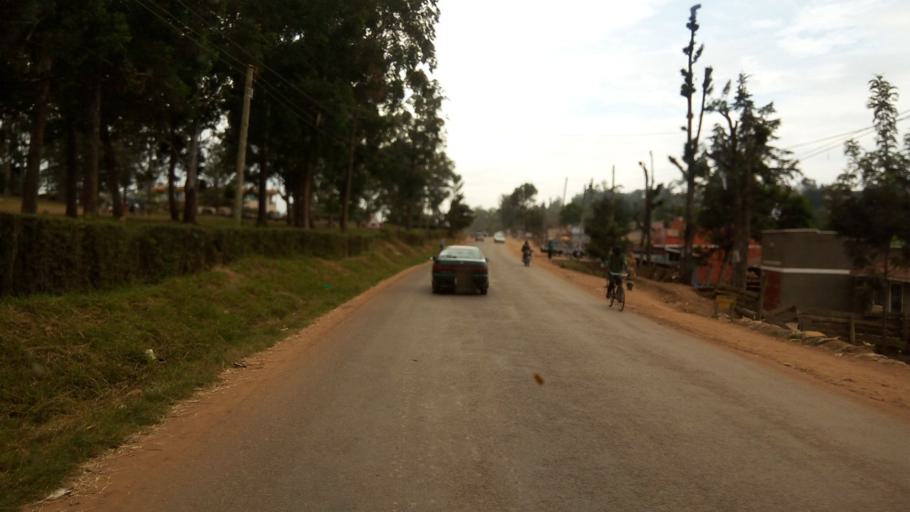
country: UG
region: Western Region
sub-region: Mbarara District
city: Mbarara
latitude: -0.6028
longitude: 30.6513
